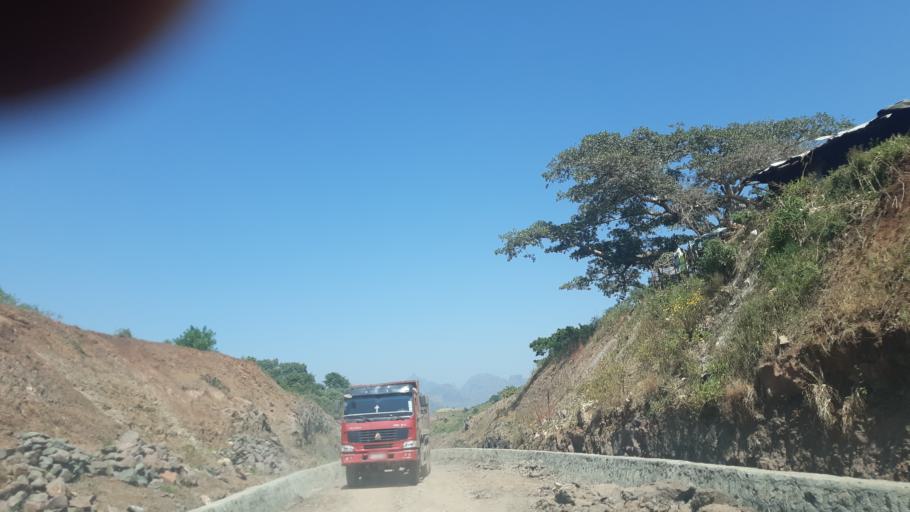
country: ET
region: Amhara
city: Dabat
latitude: 13.1633
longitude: 37.6062
